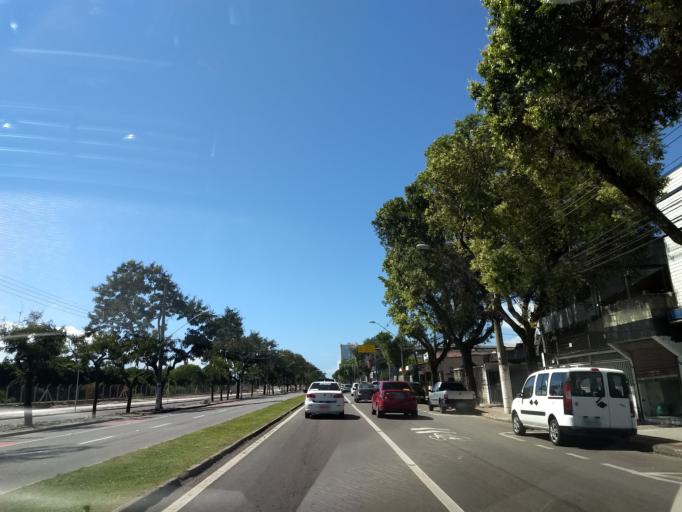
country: BR
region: Espirito Santo
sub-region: Vila Velha
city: Vila Velha
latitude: -20.2685
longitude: -40.2928
